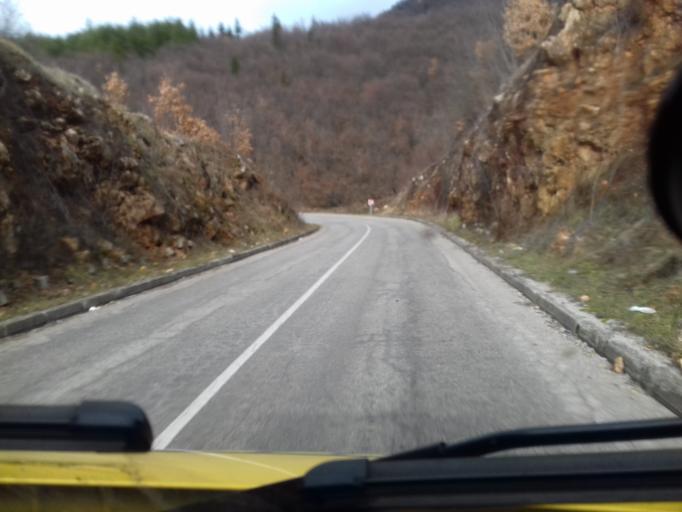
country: BA
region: Federation of Bosnia and Herzegovina
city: Turbe
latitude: 44.2644
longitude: 17.5342
